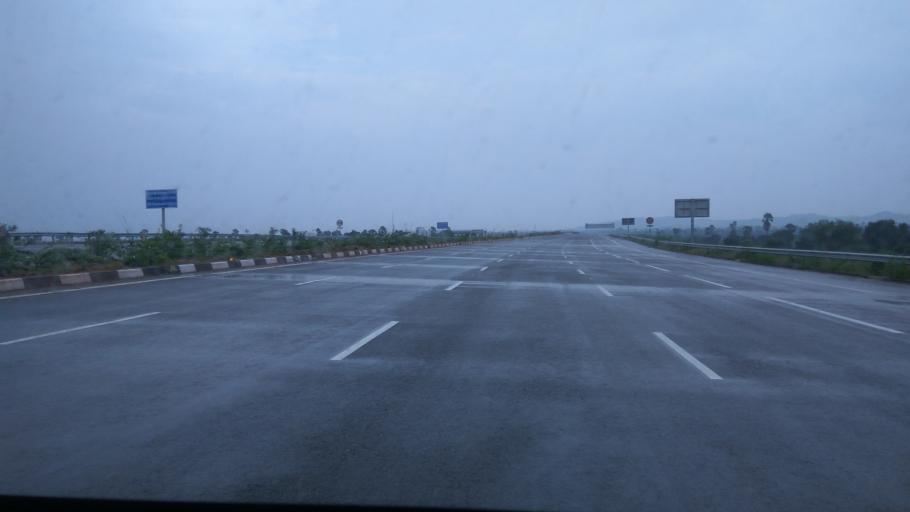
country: IN
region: Telangana
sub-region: Rangareddi
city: Ghatkesar
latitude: 17.4488
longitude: 78.6679
